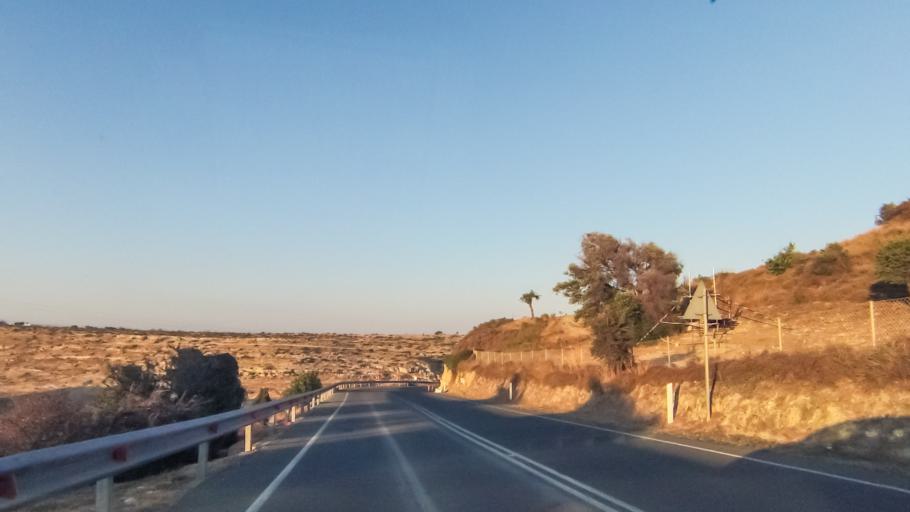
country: CY
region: Limassol
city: Erimi
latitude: 34.6689
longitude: 32.8826
